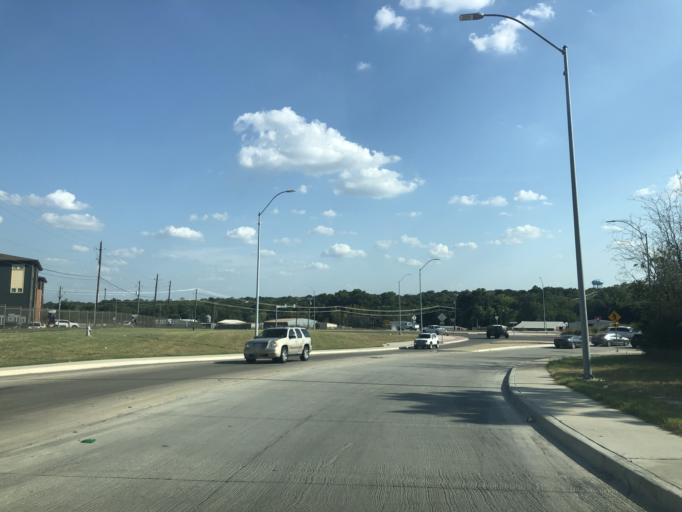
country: US
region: Texas
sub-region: Tarrant County
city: Sansom Park
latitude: 32.8180
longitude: -97.3794
